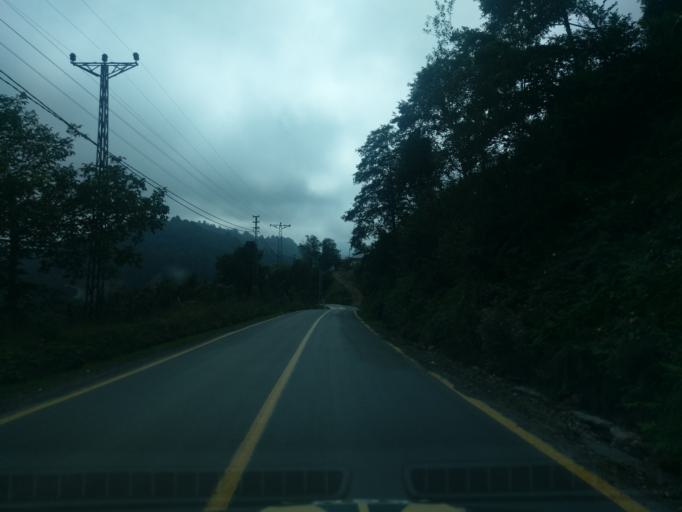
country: TR
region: Ordu
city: Gurgentepe
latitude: 40.8499
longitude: 37.6567
